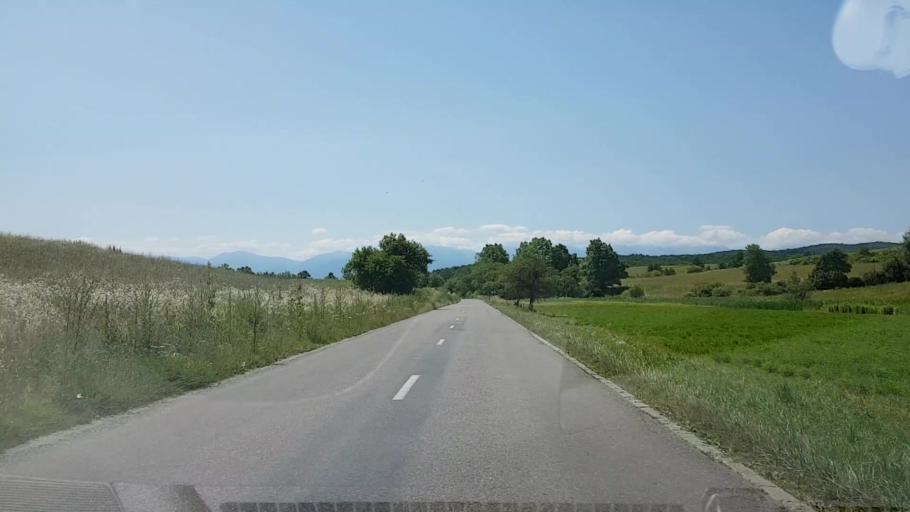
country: RO
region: Brasov
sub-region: Comuna Cincu
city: Cincu
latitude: 45.8944
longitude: 24.8116
